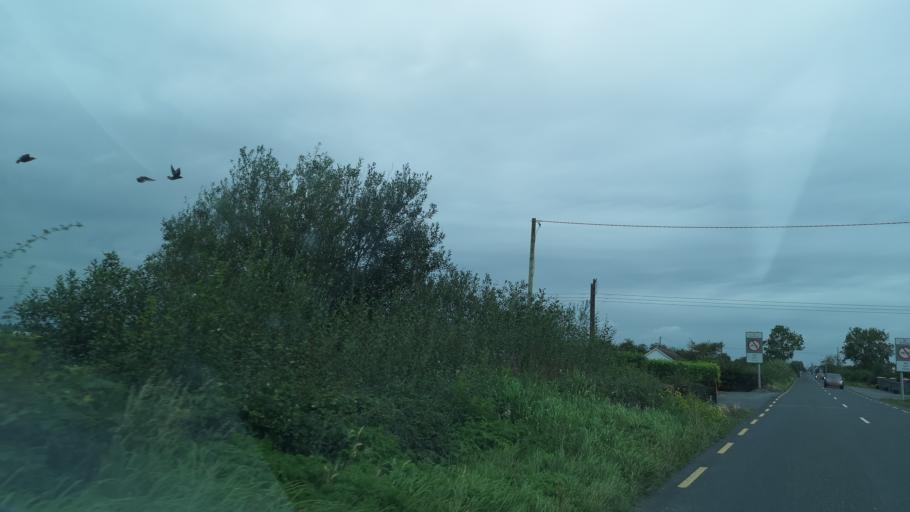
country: IE
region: Leinster
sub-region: Uibh Fhaili
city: Ferbane
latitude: 53.2181
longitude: -7.8940
